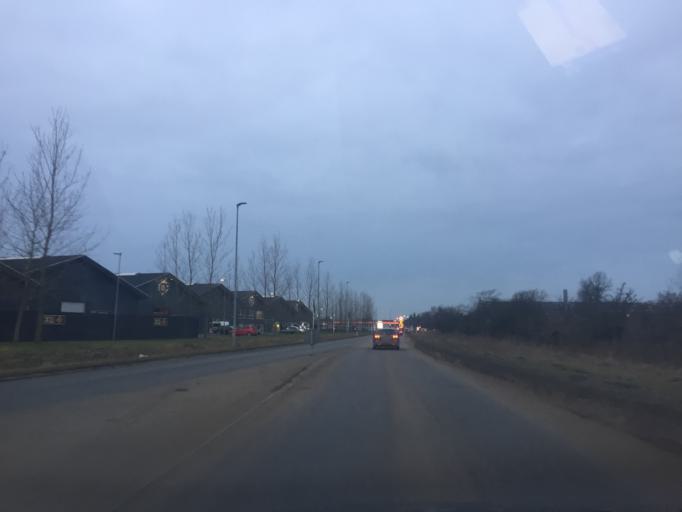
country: DK
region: Zealand
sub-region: Koge Kommune
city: Koge
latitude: 55.4797
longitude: 12.1914
